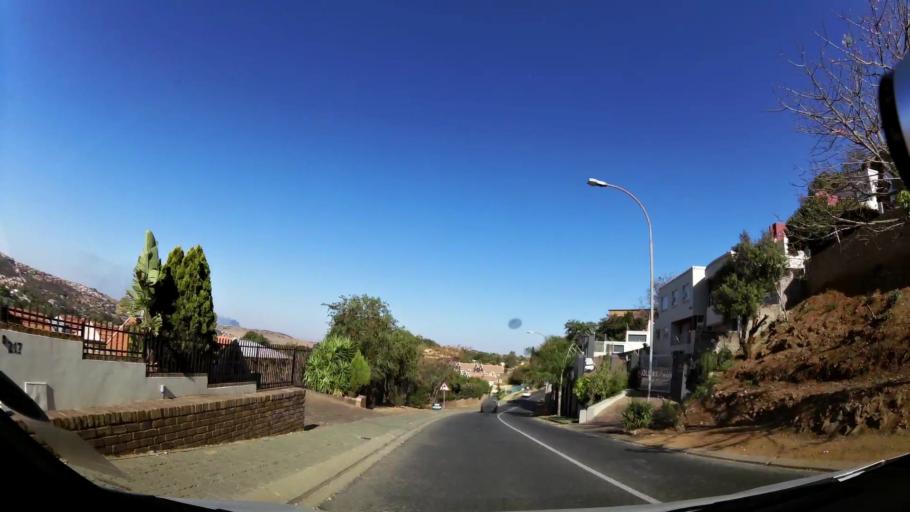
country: ZA
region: Gauteng
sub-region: City of Johannesburg Metropolitan Municipality
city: Johannesburg
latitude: -26.2806
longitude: 28.0545
